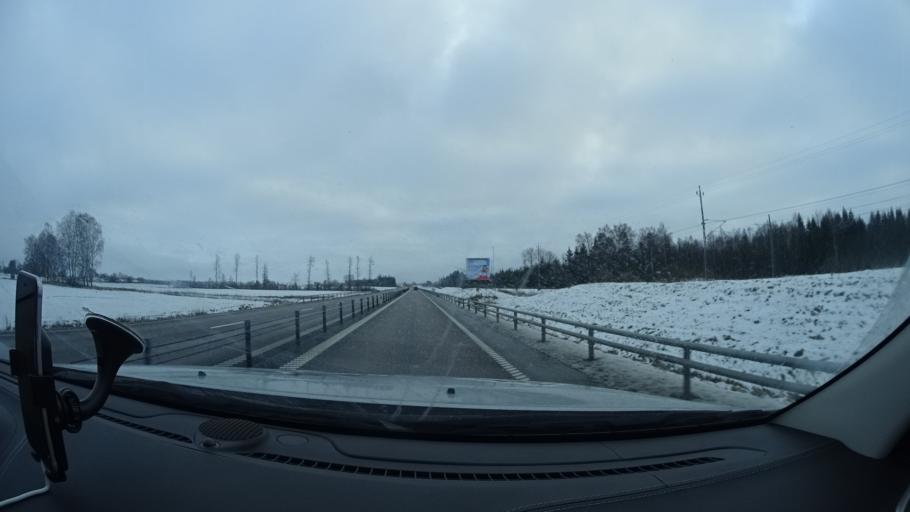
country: SE
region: OEstergoetland
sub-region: Motala Kommun
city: Stenstorp
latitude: 58.4206
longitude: 15.0713
